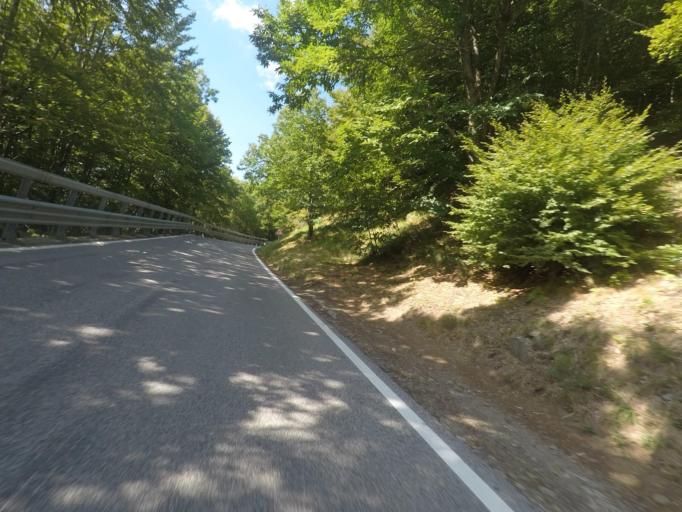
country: IT
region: Tuscany
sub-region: Provincia di Massa-Carrara
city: Comano
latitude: 44.2885
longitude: 10.2054
